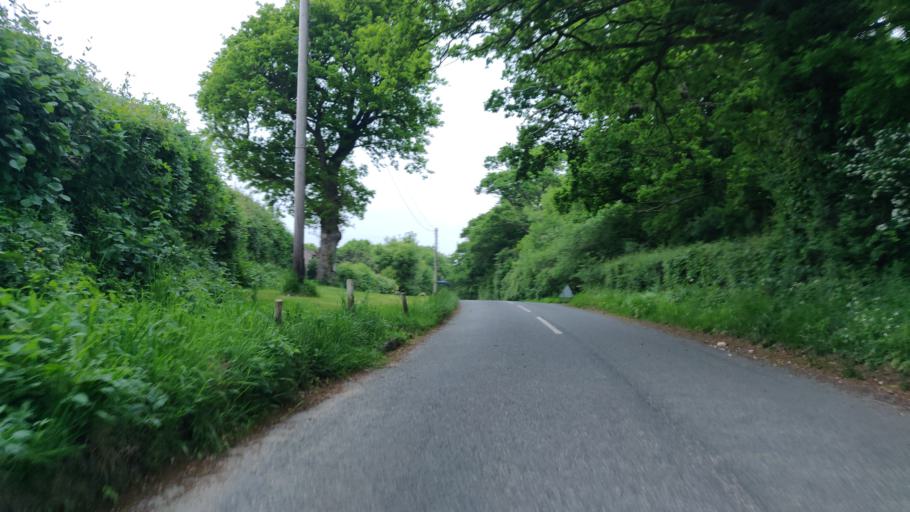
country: GB
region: England
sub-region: West Sussex
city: Partridge Green
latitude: 50.9792
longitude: -0.3013
